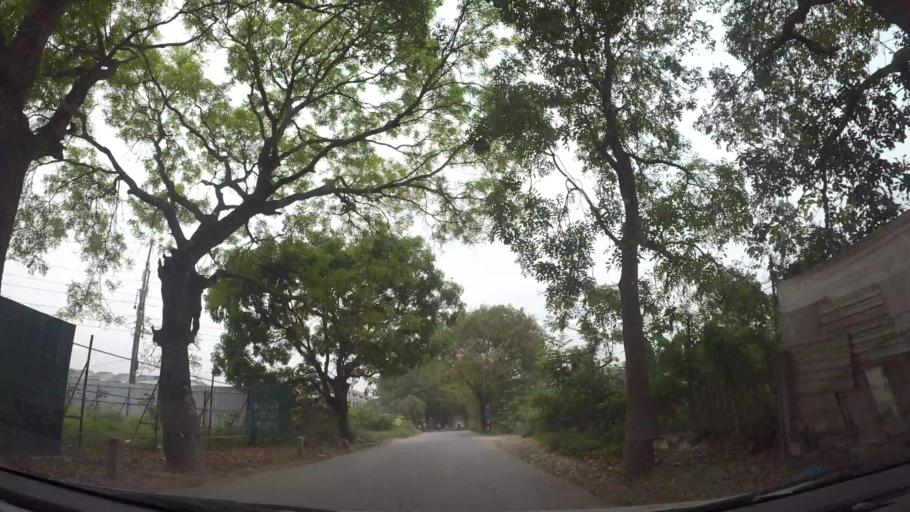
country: VN
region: Ha Noi
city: Cau Dien
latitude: 21.0235
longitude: 105.7425
